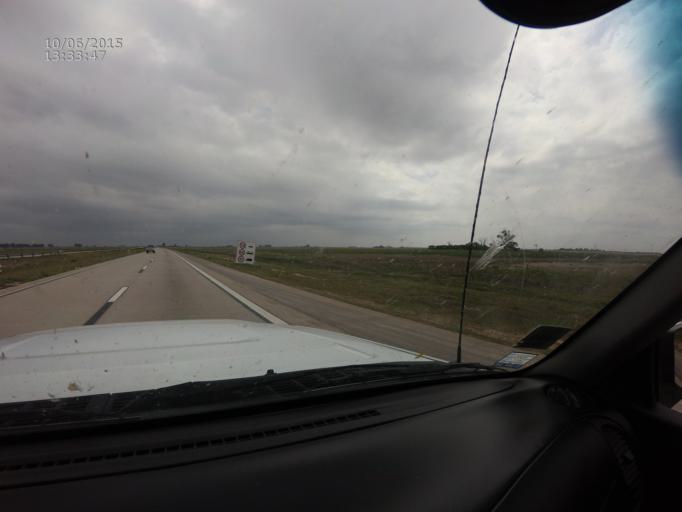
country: AR
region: Cordoba
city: Leones
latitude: -32.6219
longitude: -62.3355
